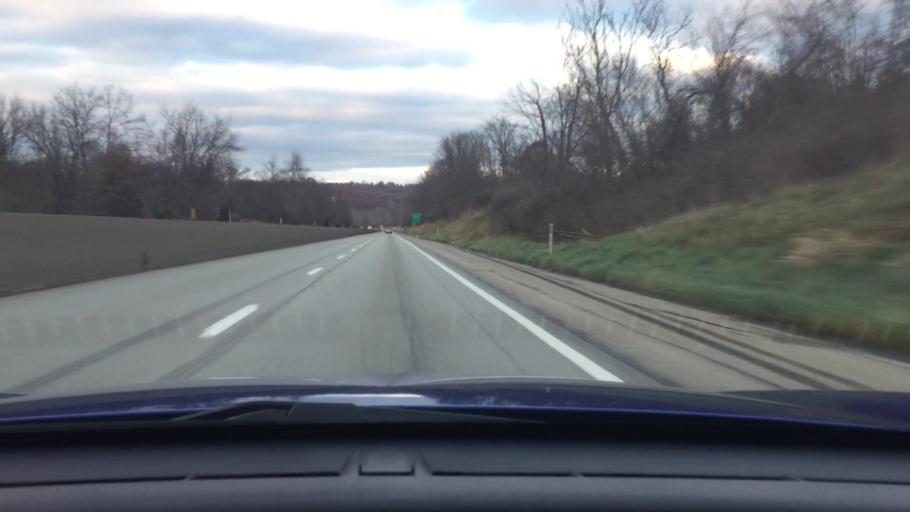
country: US
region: Pennsylvania
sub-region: Westmoreland County
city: New Stanton
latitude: 40.2023
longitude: -79.6811
